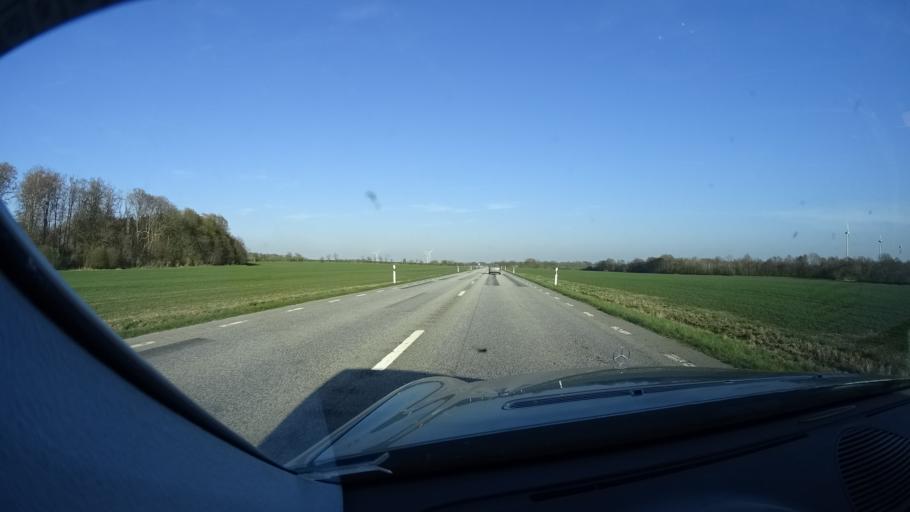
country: SE
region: Skane
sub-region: Eslovs Kommun
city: Stehag
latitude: 55.8488
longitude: 13.4302
